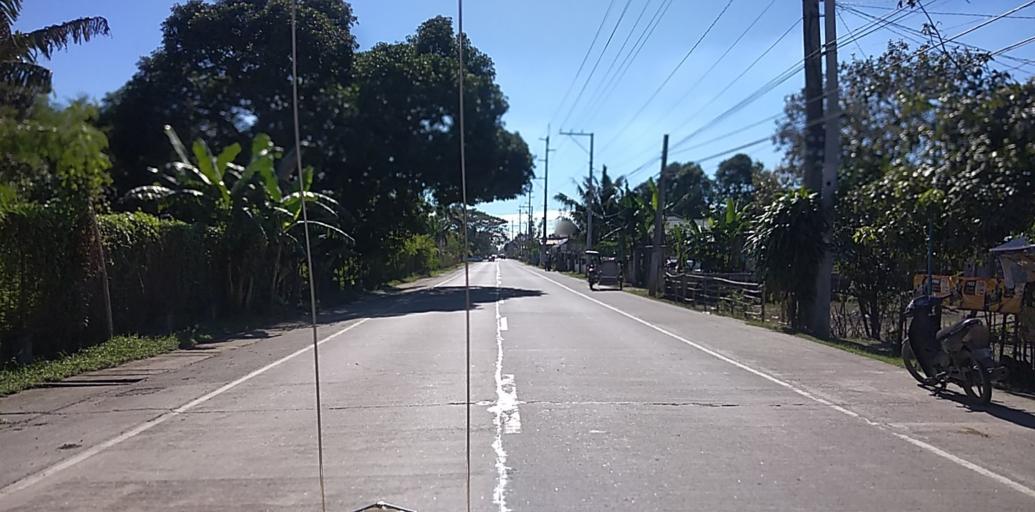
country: PH
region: Central Luzon
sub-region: Province of Pampanga
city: Santo Domingo
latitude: 15.0627
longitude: 120.7708
